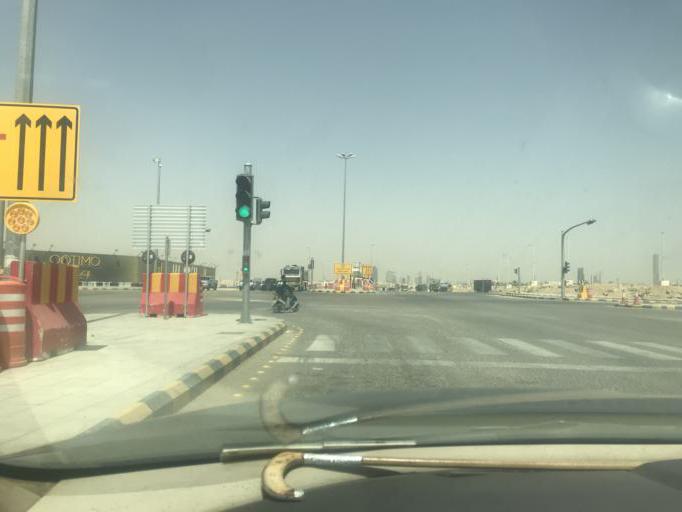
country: SA
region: Ar Riyad
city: Riyadh
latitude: 24.7949
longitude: 46.5862
